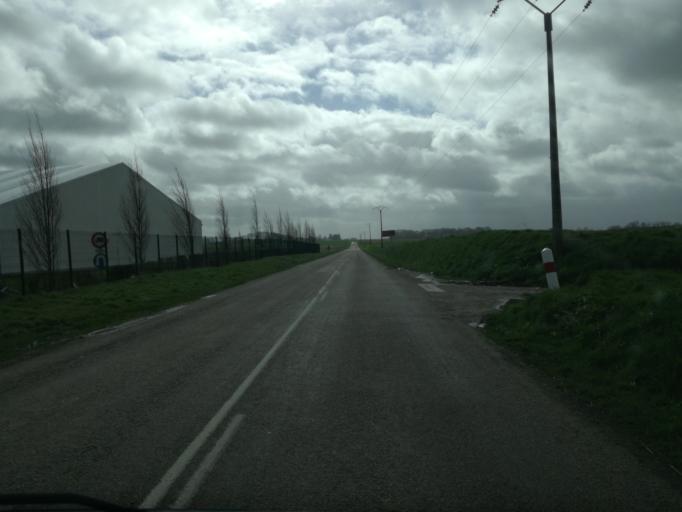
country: FR
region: Haute-Normandie
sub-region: Departement de la Seine-Maritime
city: Valliquerville
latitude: 49.6087
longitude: 0.6662
